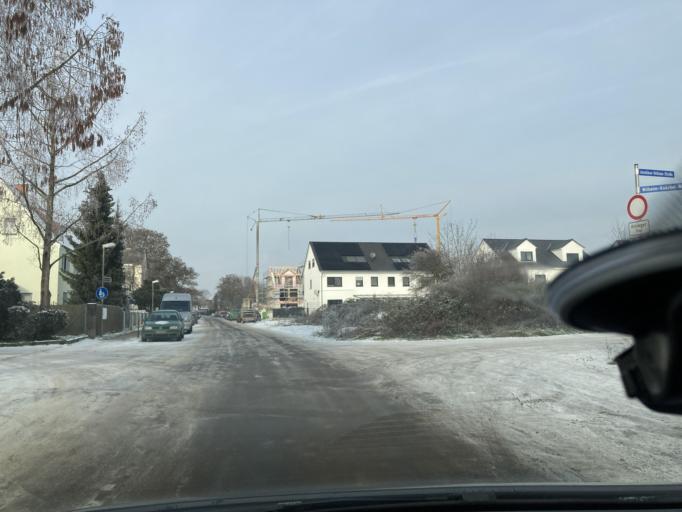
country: DE
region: Hesse
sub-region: Regierungsbezirk Darmstadt
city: Offenbach
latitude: 50.1183
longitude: 8.7896
